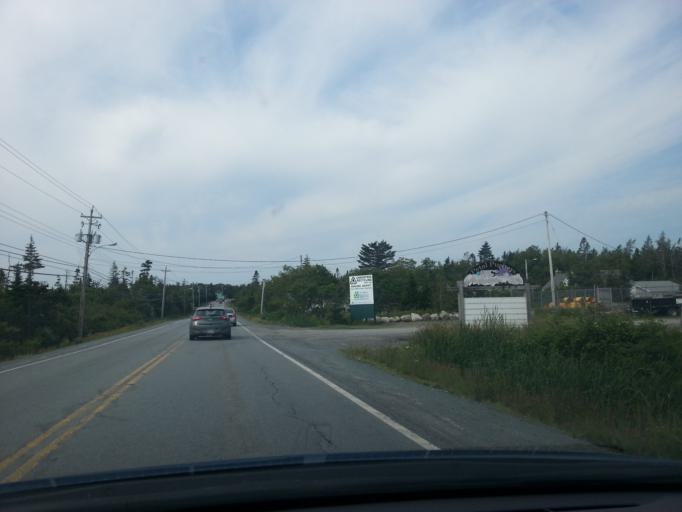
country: CA
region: Nova Scotia
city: Halifax
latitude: 44.6001
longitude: -63.6845
